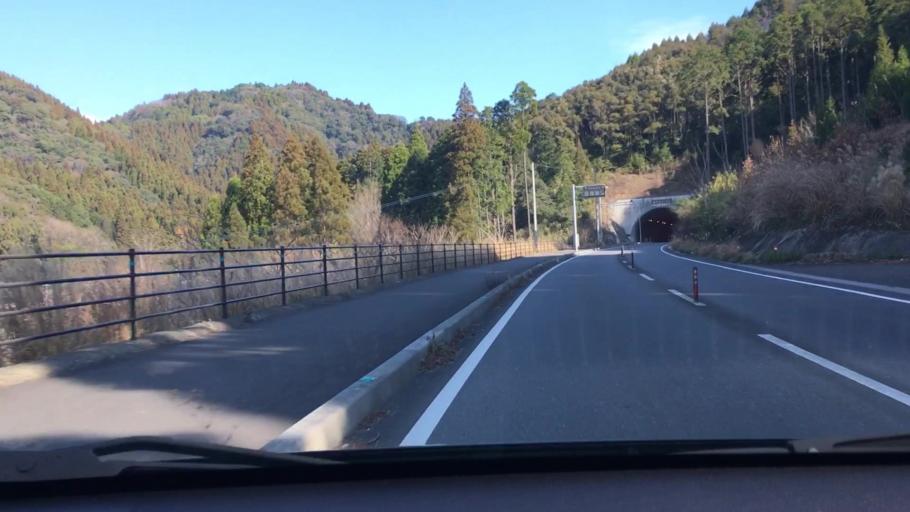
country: JP
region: Oita
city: Saiki
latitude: 32.9599
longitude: 131.8476
